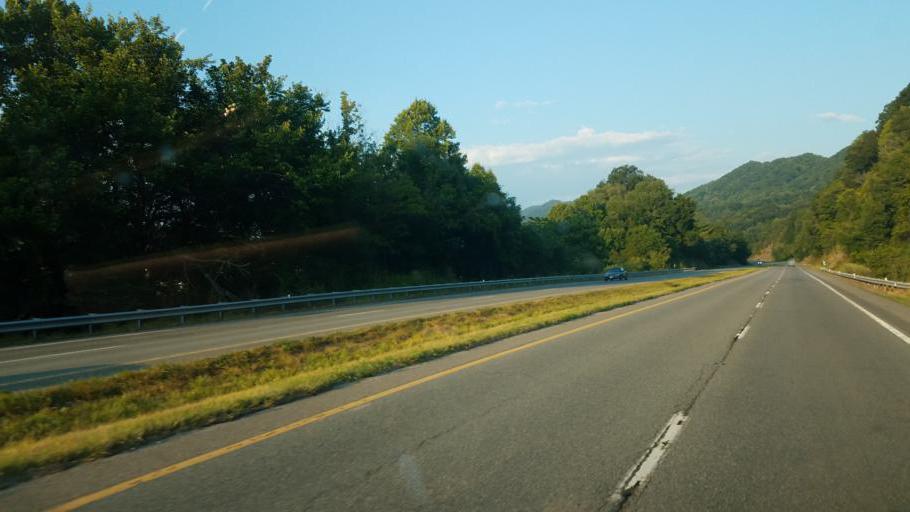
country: US
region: Virginia
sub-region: Scott County
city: Gate City
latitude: 36.6311
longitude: -82.5962
